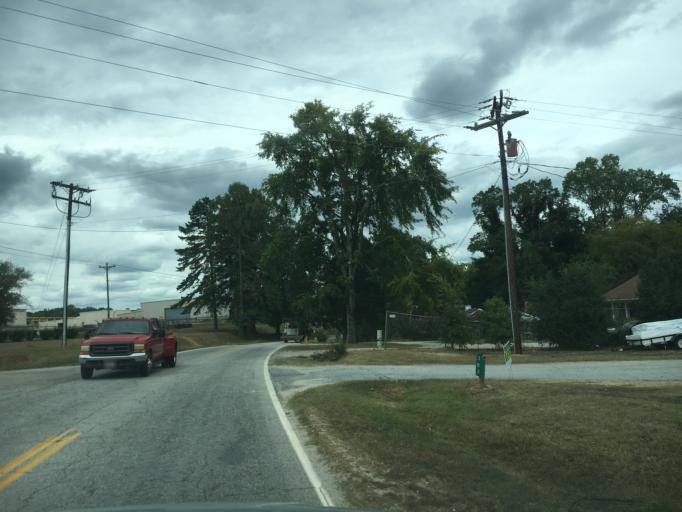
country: US
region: South Carolina
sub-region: Laurens County
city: Watts Mills
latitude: 34.5028
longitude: -81.9729
